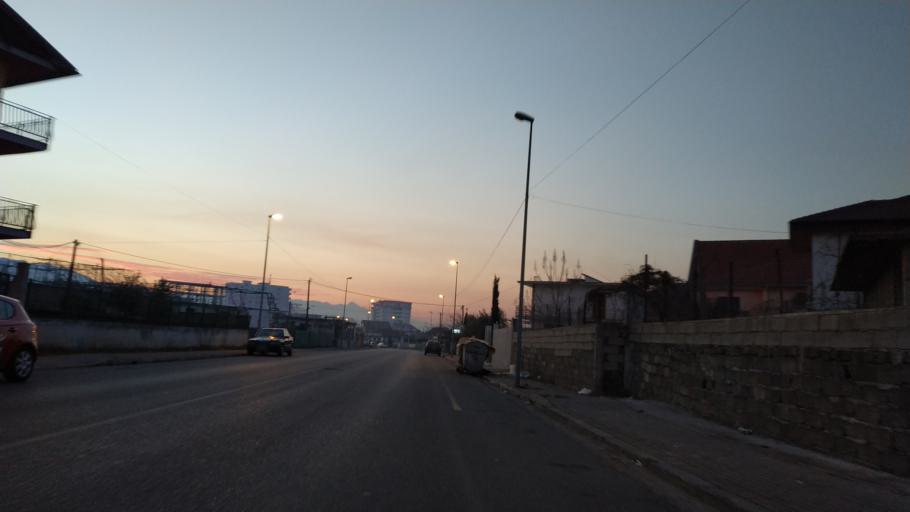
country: AL
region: Shkoder
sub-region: Rrethi i Shkodres
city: Shkoder
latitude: 42.0789
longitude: 19.5214
